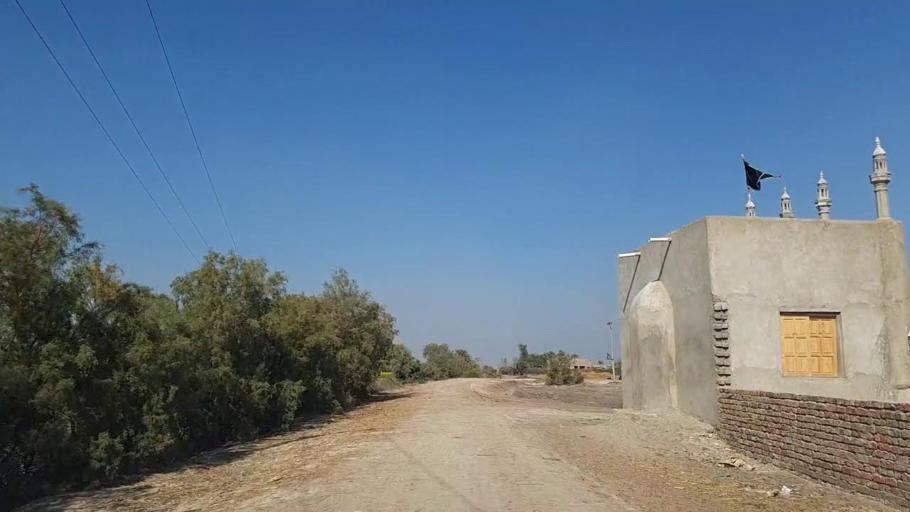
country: PK
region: Sindh
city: Bandhi
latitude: 26.5471
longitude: 68.3270
